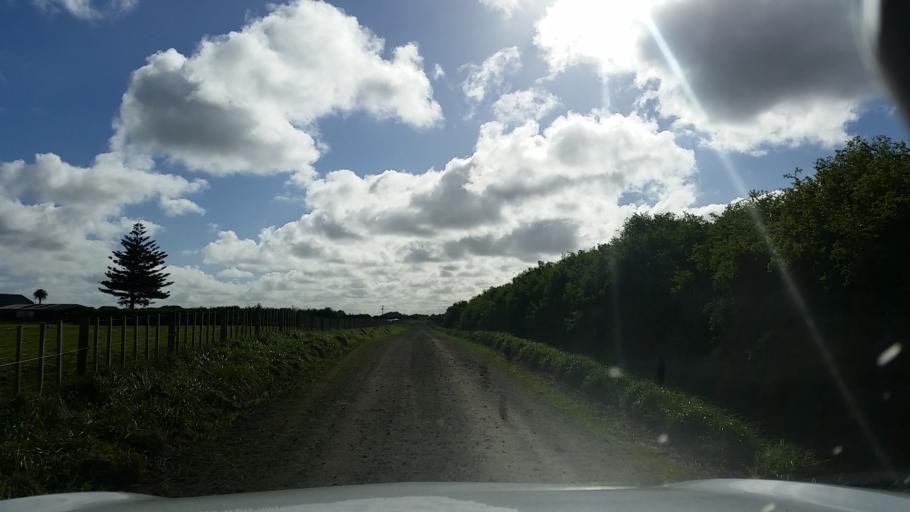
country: NZ
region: Taranaki
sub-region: South Taranaki District
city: Patea
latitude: -39.7499
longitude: 174.5188
